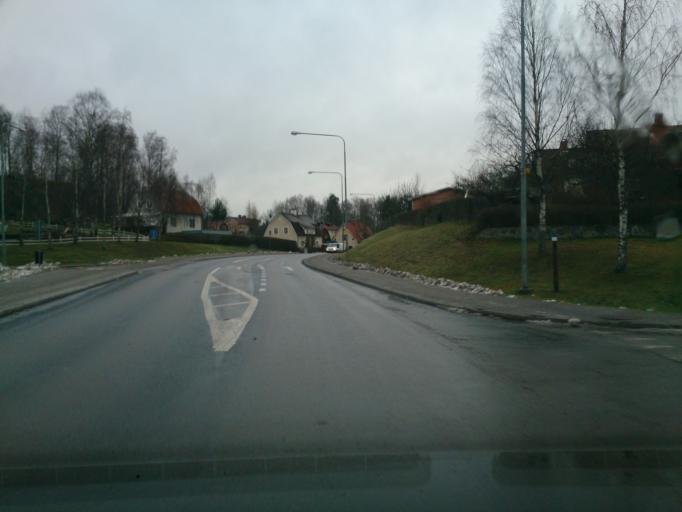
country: SE
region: OEstergoetland
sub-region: Atvidabergs Kommun
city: Atvidaberg
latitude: 58.2025
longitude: 16.0066
